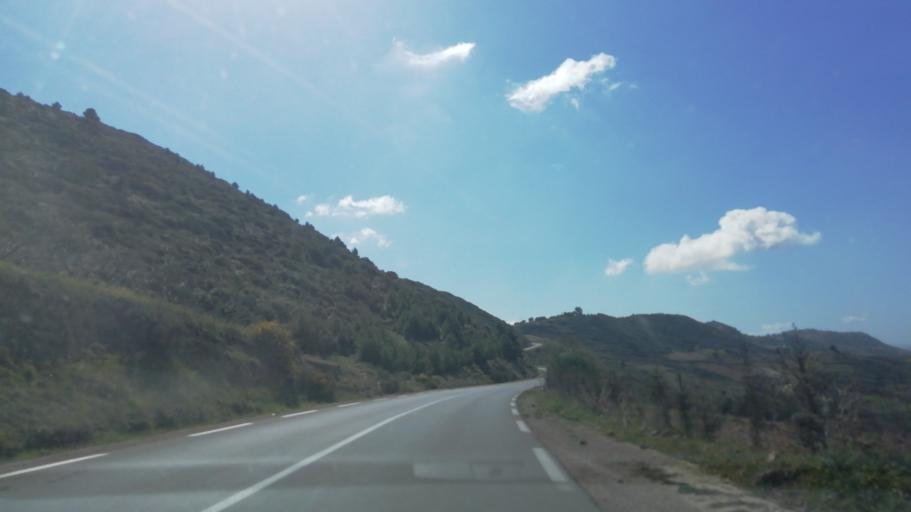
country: DZ
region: Mascara
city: Mascara
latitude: 35.4669
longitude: 0.1529
